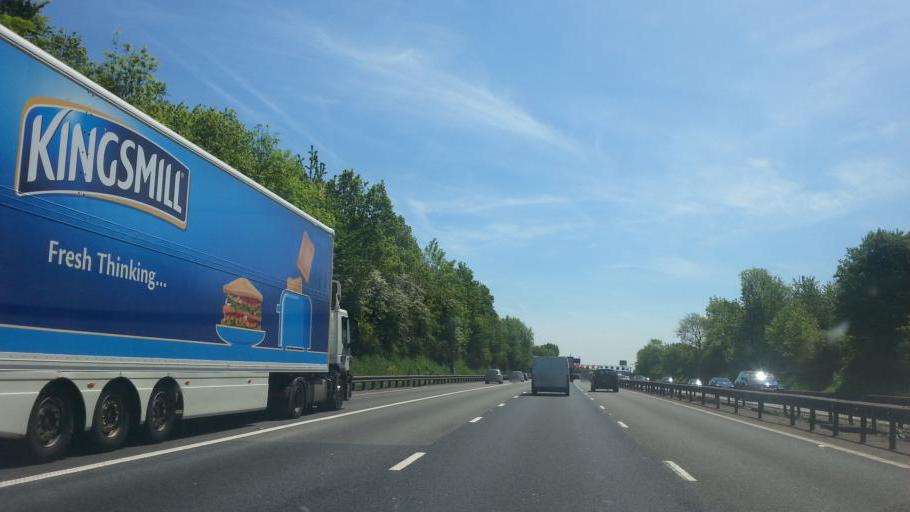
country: GB
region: England
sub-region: Central Bedfordshire
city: Caddington
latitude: 51.8787
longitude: -0.4505
